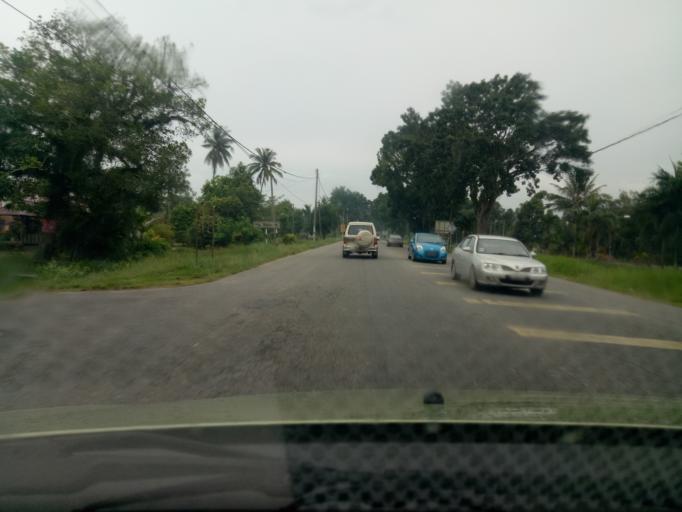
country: MY
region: Kedah
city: Gurun
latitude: 5.8990
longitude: 100.4365
